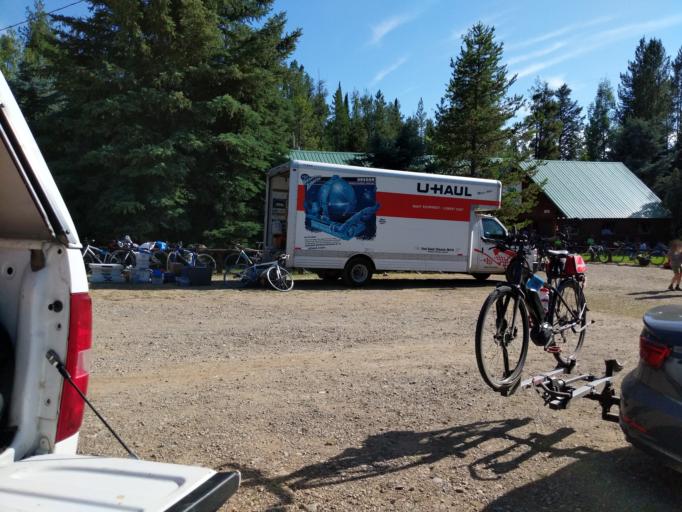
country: US
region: Wyoming
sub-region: Teton County
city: Hoback
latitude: 43.1955
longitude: -111.0316
